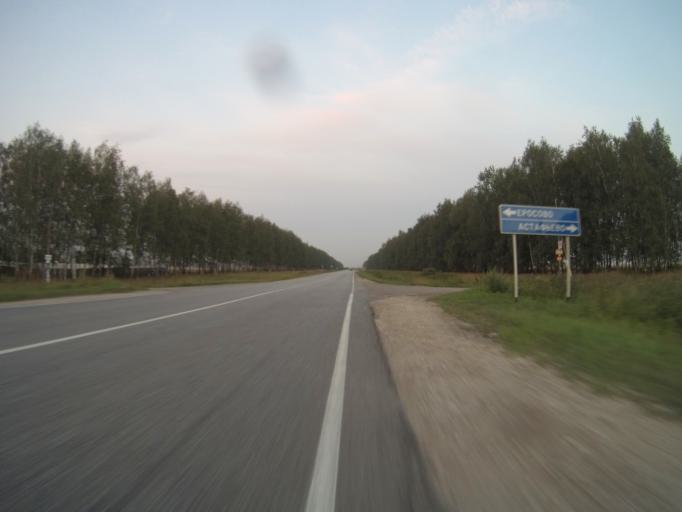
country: RU
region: Vladimir
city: Stavrovo
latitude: 56.1148
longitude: 40.0617
